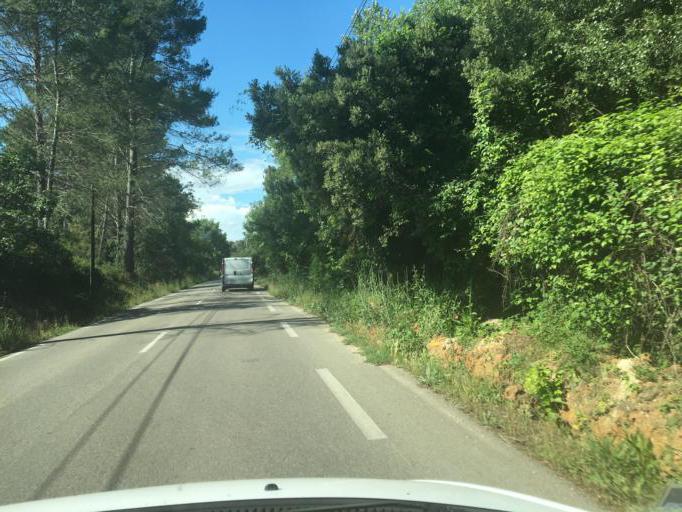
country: FR
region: Provence-Alpes-Cote d'Azur
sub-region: Departement des Bouches-du-Rhone
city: Eguilles
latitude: 43.5255
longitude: 5.3517
